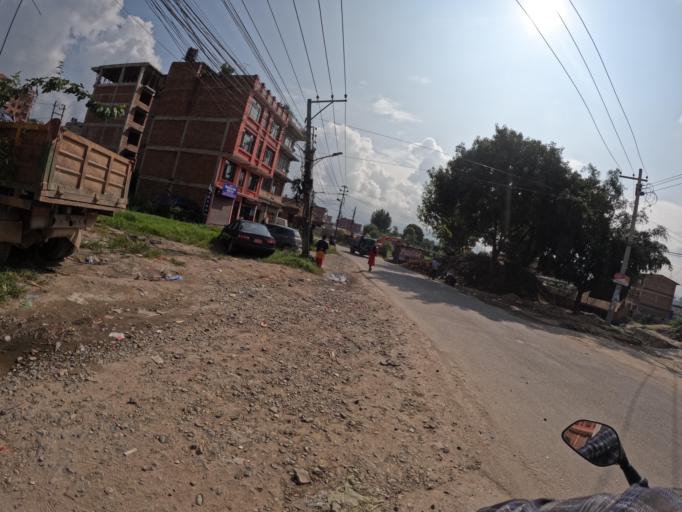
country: NP
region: Central Region
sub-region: Bagmati Zone
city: Bhaktapur
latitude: 27.6742
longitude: 85.4432
